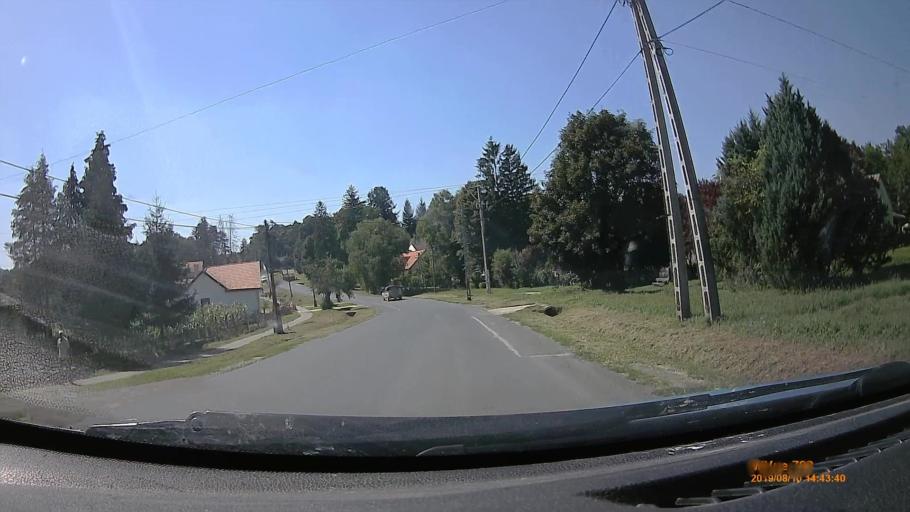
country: HU
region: Somogy
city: Somogyvar
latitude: 46.5798
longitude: 17.6527
